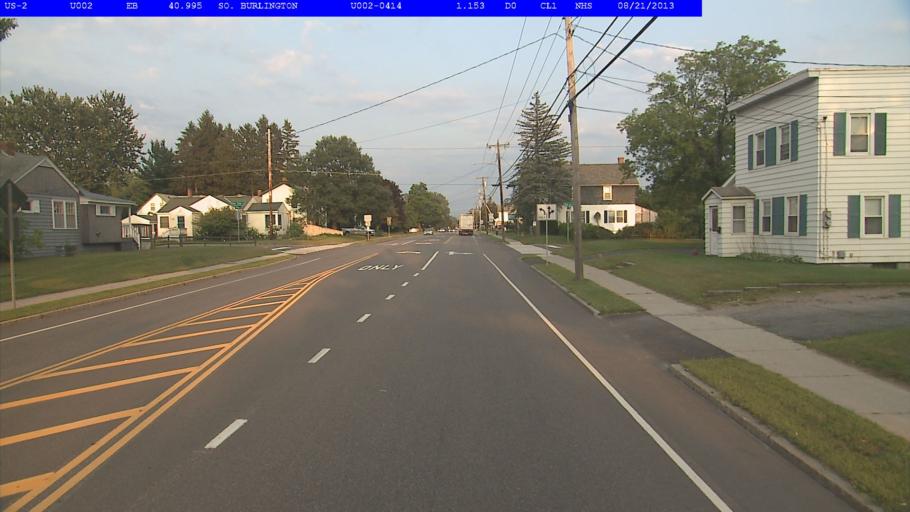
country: US
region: Vermont
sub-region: Chittenden County
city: South Burlington
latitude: 44.4664
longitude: -73.1687
